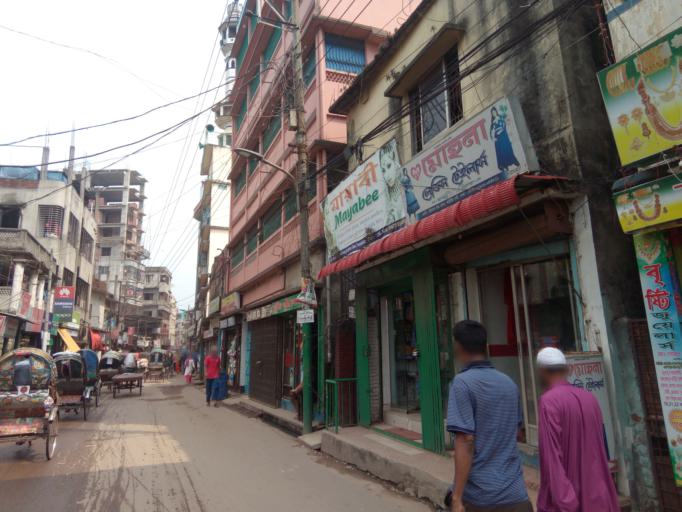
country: BD
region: Dhaka
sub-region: Dhaka
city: Dhaka
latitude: 23.6952
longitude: 90.4247
